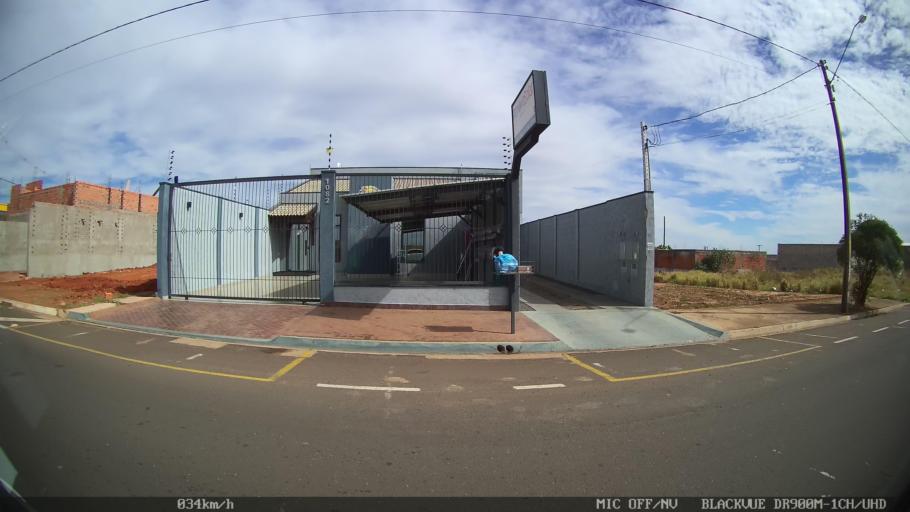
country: BR
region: Sao Paulo
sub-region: Catanduva
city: Catanduva
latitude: -21.1597
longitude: -48.9630
